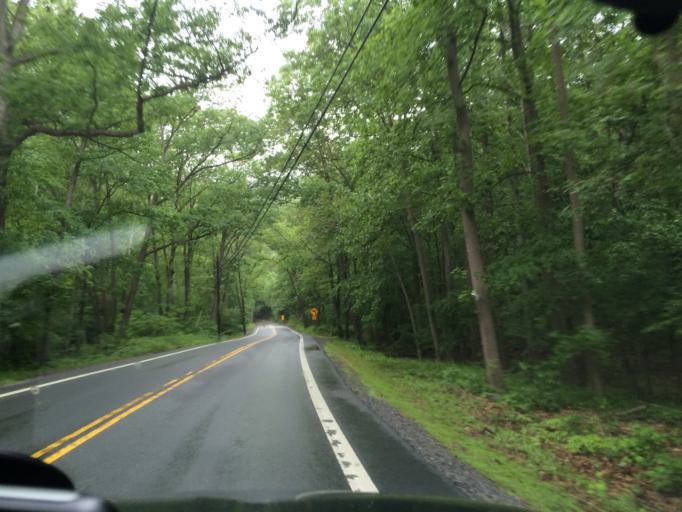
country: US
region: Maryland
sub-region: Frederick County
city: Thurmont
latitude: 39.6489
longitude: -77.4205
